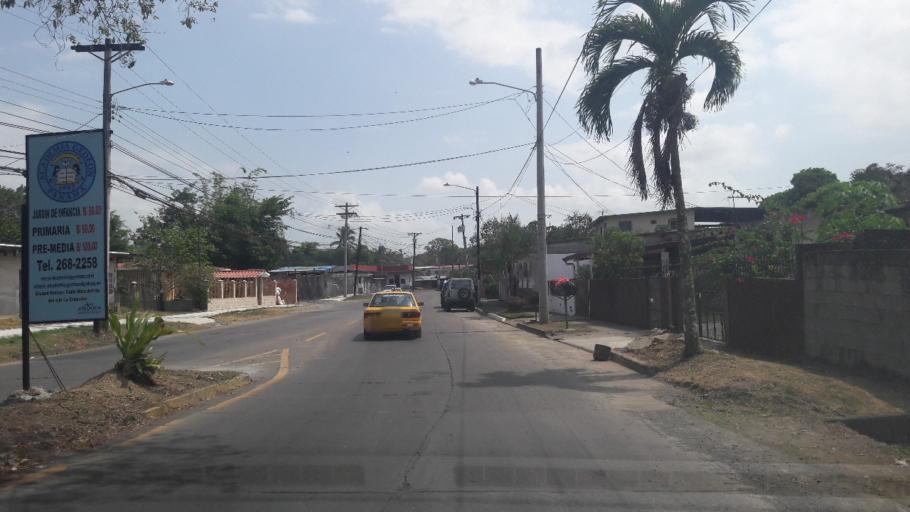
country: PA
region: Panama
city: Alcalde Diaz
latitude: 9.1295
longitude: -79.5470
